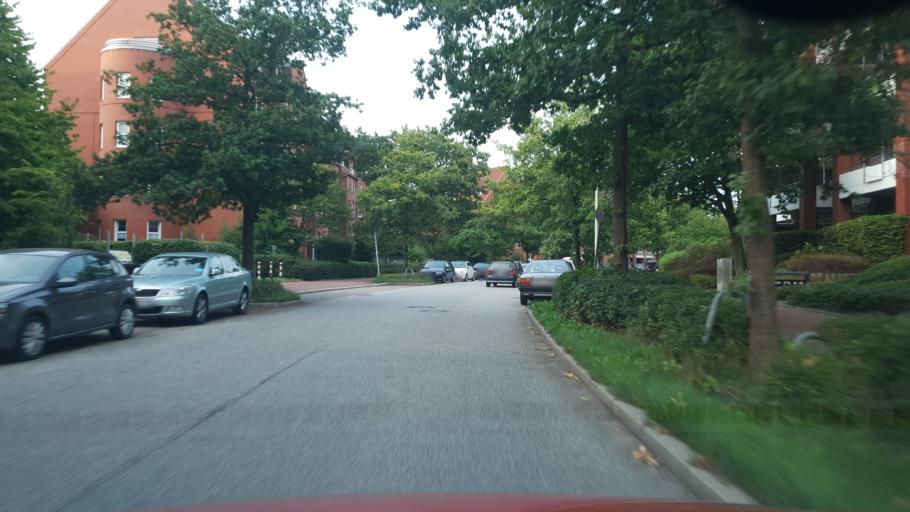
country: DE
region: Schleswig-Holstein
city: Kronshagen
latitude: 54.3462
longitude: 10.1028
